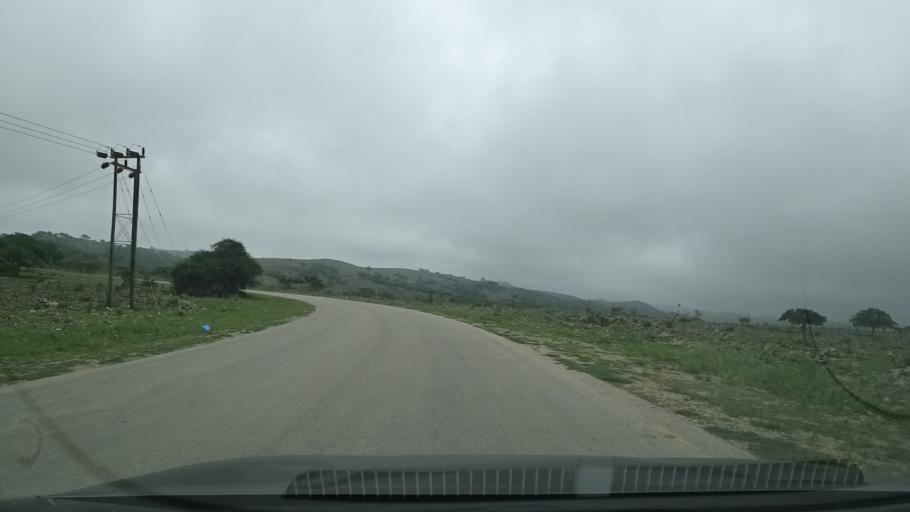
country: OM
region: Zufar
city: Salalah
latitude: 17.1170
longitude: 54.5735
